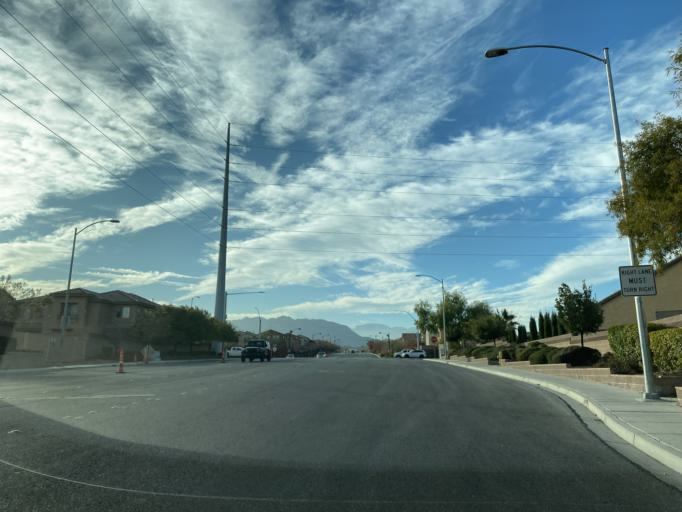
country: US
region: Nevada
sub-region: Clark County
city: Summerlin South
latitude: 36.2995
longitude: -115.3138
